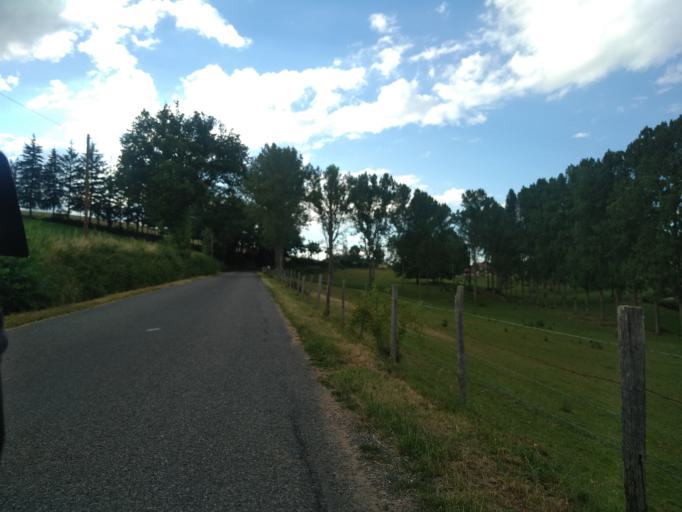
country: FR
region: Rhone-Alpes
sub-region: Departement de la Loire
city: Panissieres
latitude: 45.7423
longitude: 4.3506
